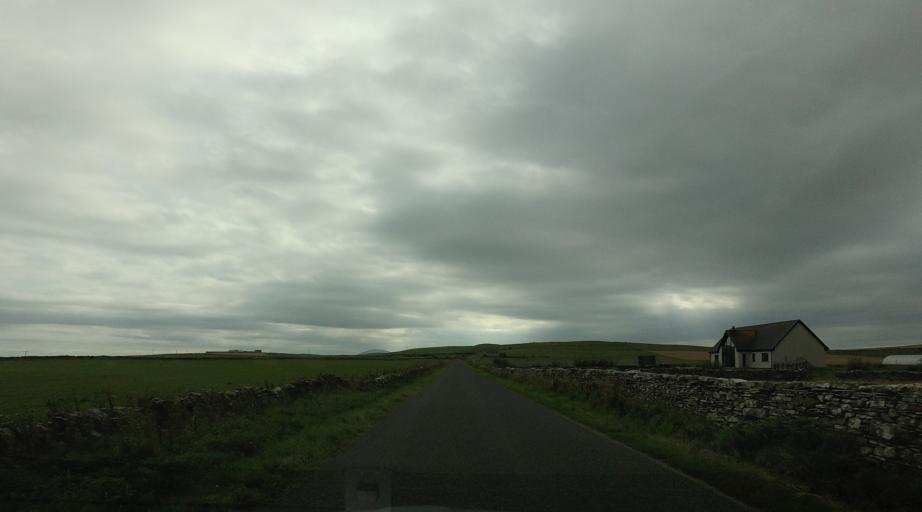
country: GB
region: Scotland
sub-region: Orkney Islands
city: Stromness
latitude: 59.0343
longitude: -3.3127
